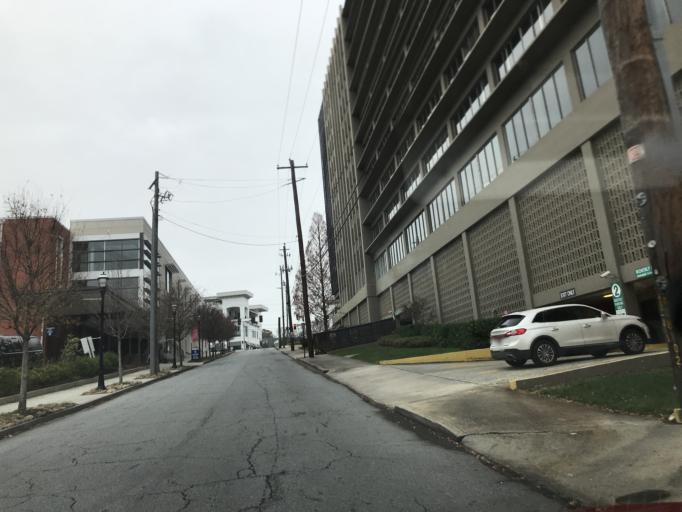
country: US
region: Georgia
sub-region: Fulton County
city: Atlanta
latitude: 33.8012
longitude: -84.3942
